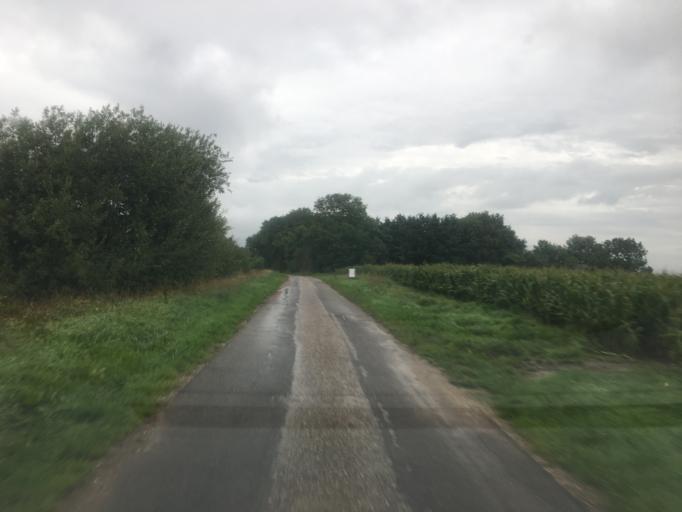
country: DK
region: South Denmark
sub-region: Tonder Kommune
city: Tonder
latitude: 54.9770
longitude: 8.9075
